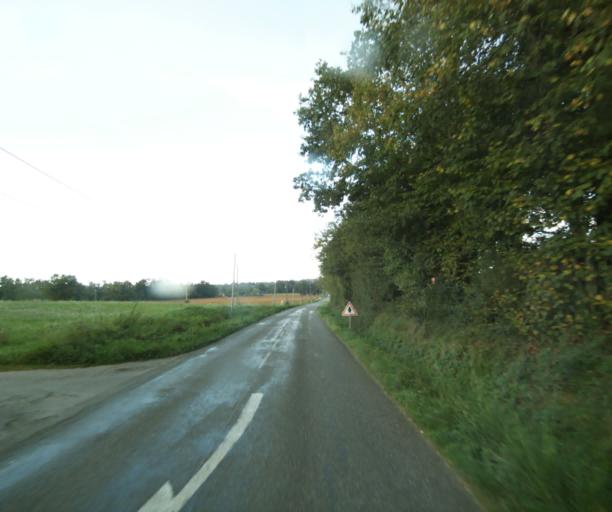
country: FR
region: Midi-Pyrenees
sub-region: Departement du Gers
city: Cazaubon
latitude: 43.9194
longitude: -0.0785
